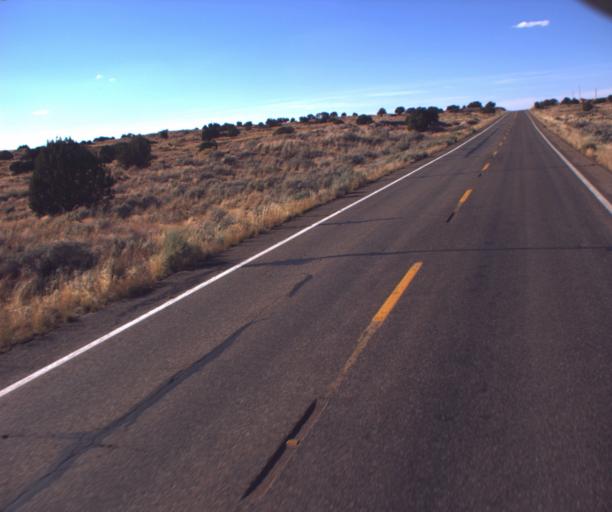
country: US
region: Arizona
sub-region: Coconino County
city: Kaibito
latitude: 36.5910
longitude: -111.1578
